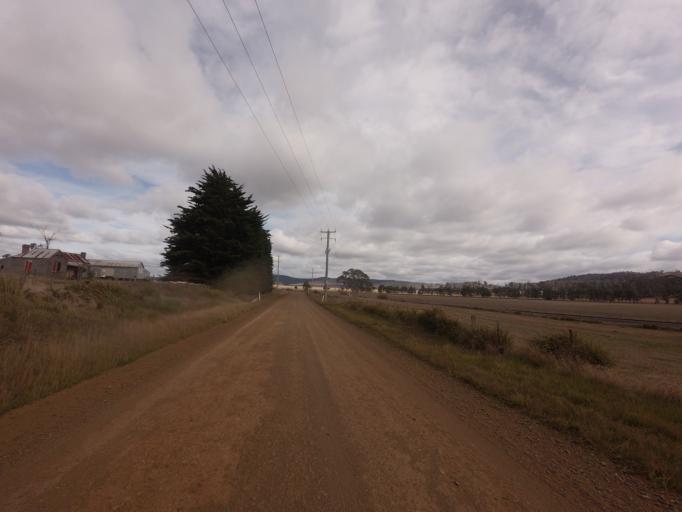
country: AU
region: Tasmania
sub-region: Brighton
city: Bridgewater
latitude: -42.3986
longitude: 147.3917
